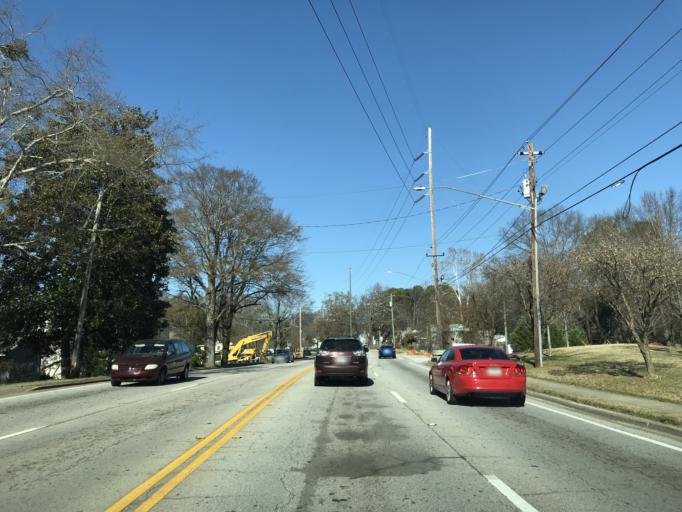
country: US
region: Georgia
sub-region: DeKalb County
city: Tucker
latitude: 33.8570
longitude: -84.2180
